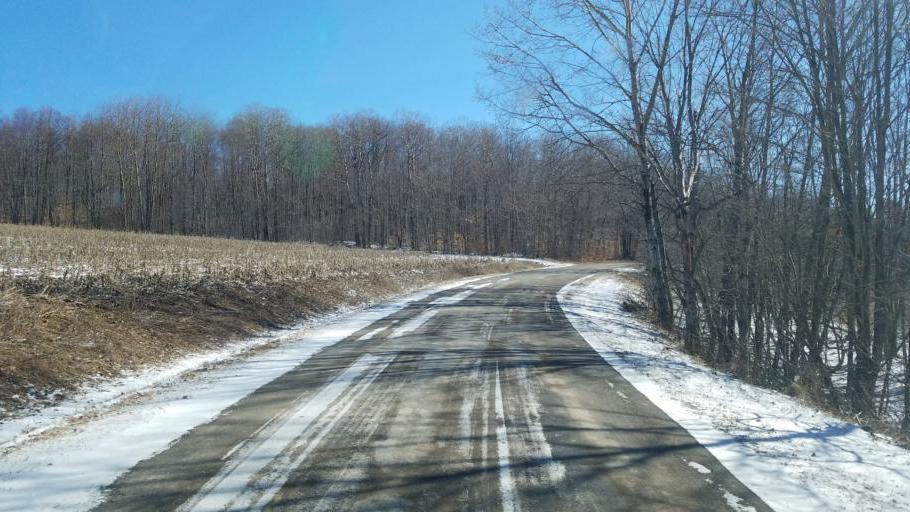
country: US
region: New York
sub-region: Allegany County
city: Wellsville
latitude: 42.0505
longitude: -77.9818
